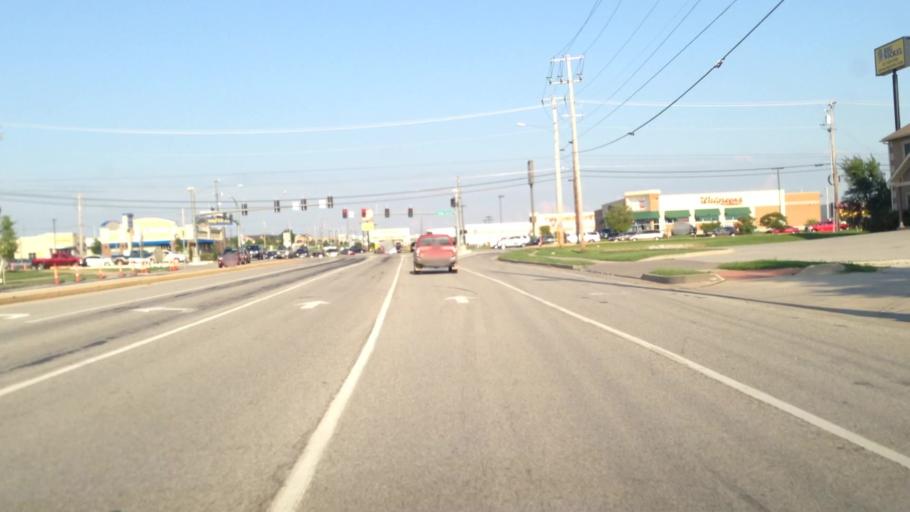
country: US
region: Missouri
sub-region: Jasper County
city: Duquesne
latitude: 37.0692
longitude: -94.4793
